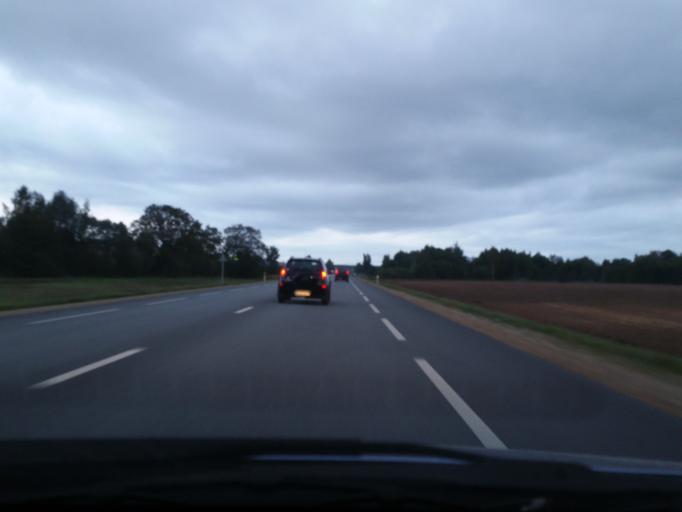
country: LV
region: Adazi
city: Adazi
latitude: 57.0851
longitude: 24.3147
